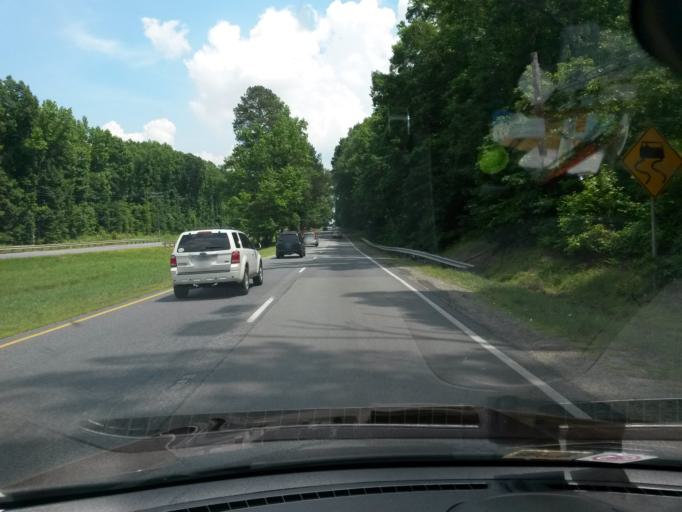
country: US
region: Virginia
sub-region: Chesterfield County
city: Enon
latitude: 37.3246
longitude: -77.3157
